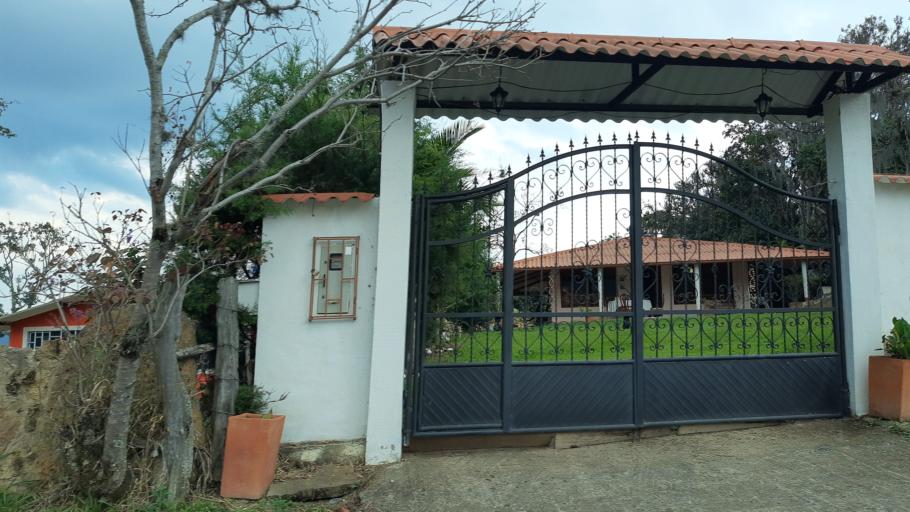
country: CO
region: Boyaca
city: Moniquira
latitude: 5.8229
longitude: -73.5960
